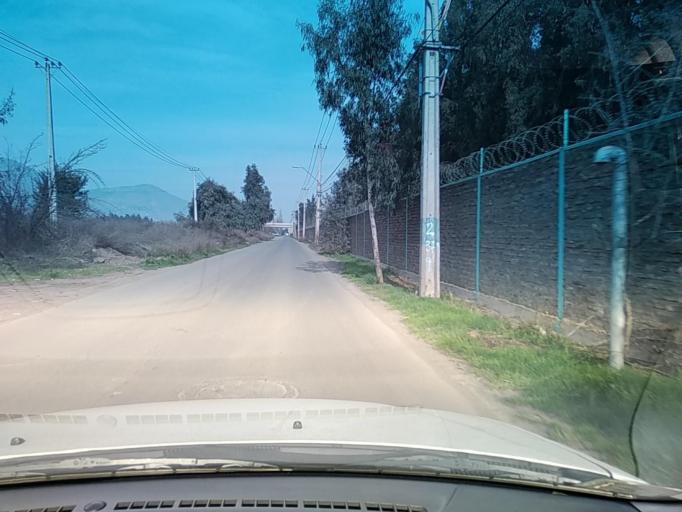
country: CL
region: Santiago Metropolitan
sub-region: Provincia de Chacabuco
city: Chicureo Abajo
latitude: -33.2936
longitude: -70.7248
